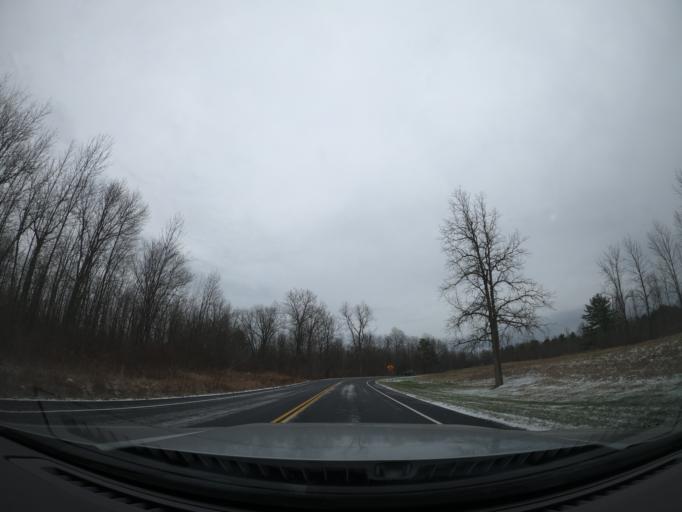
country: US
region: New York
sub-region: Tompkins County
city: Northeast Ithaca
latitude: 42.4842
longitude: -76.4555
